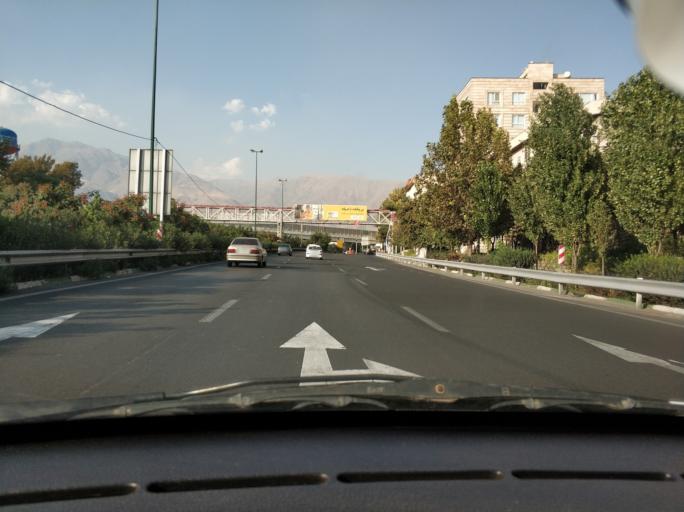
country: IR
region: Tehran
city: Tajrish
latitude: 35.7768
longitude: 51.4770
